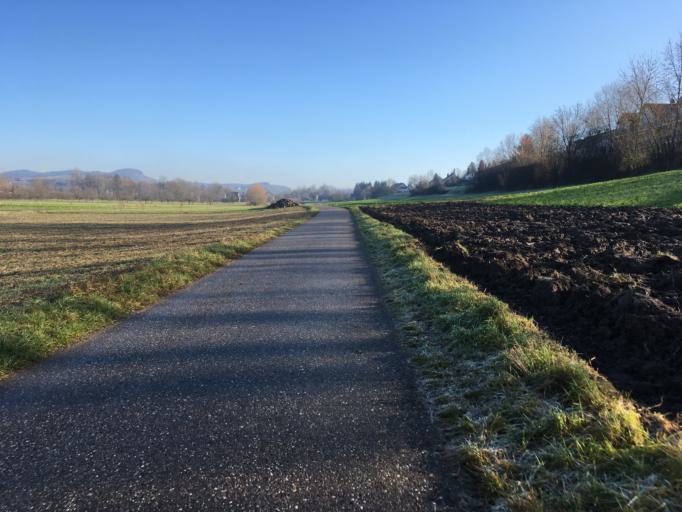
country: DE
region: Baden-Wuerttemberg
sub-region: Regierungsbezirk Stuttgart
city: Ellhofen
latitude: 49.1521
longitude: 9.3115
